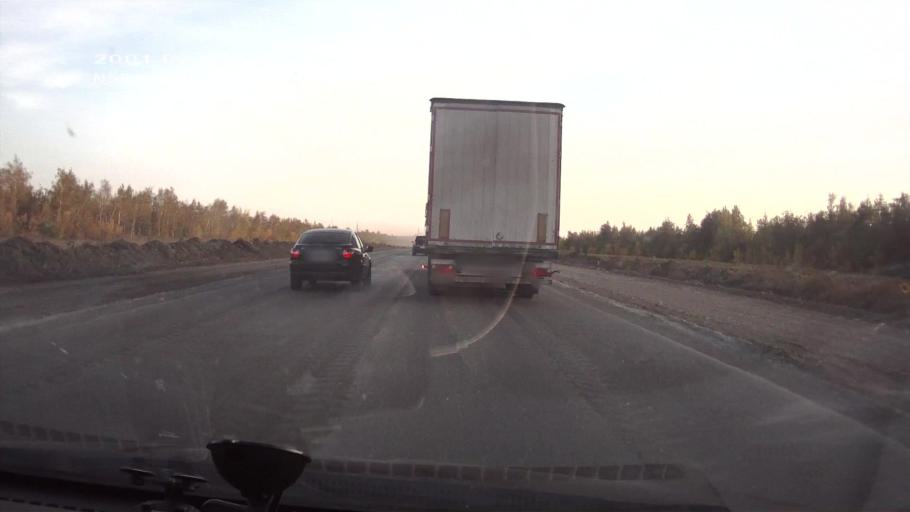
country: RU
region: Saratov
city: Kamenskiy
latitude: 50.9300
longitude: 45.5998
